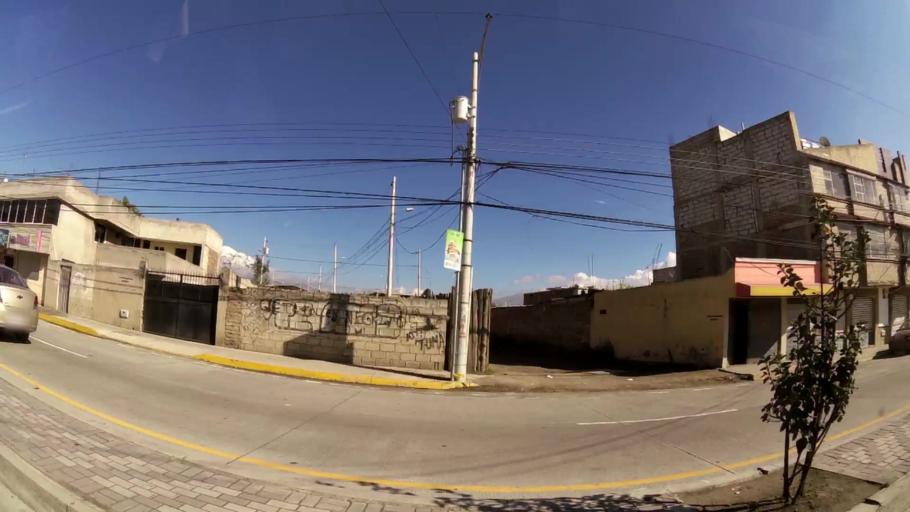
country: EC
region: Chimborazo
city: Riobamba
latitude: -1.6456
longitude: -78.6768
